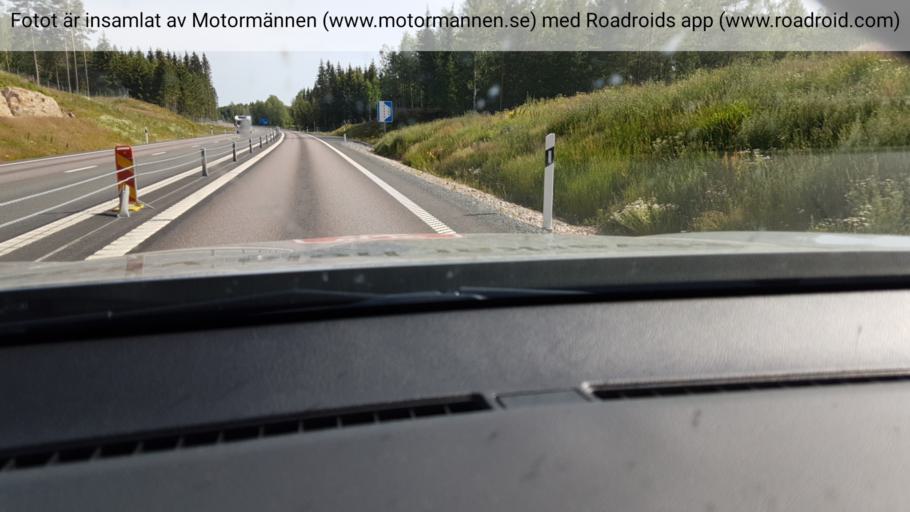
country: SE
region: Joenkoeping
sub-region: Aneby Kommun
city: Aneby
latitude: 57.8554
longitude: 14.8648
